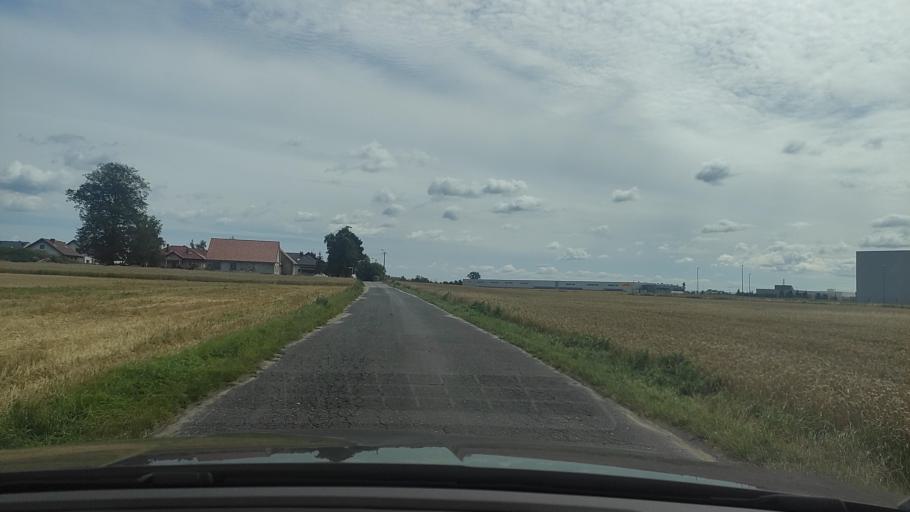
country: PL
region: Greater Poland Voivodeship
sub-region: Powiat poznanski
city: Kostrzyn
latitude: 52.4055
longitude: 17.2013
